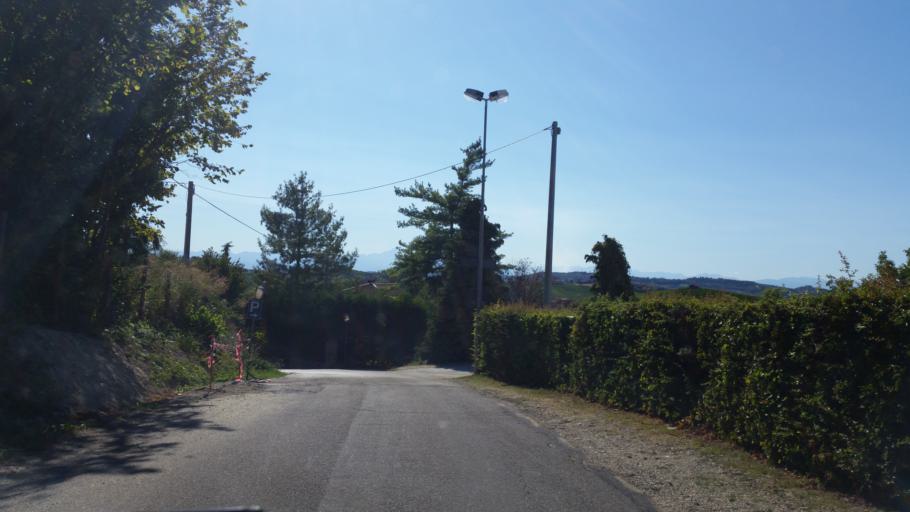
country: IT
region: Piedmont
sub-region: Provincia di Cuneo
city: Neive-Borgonovo
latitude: 44.7275
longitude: 8.1135
